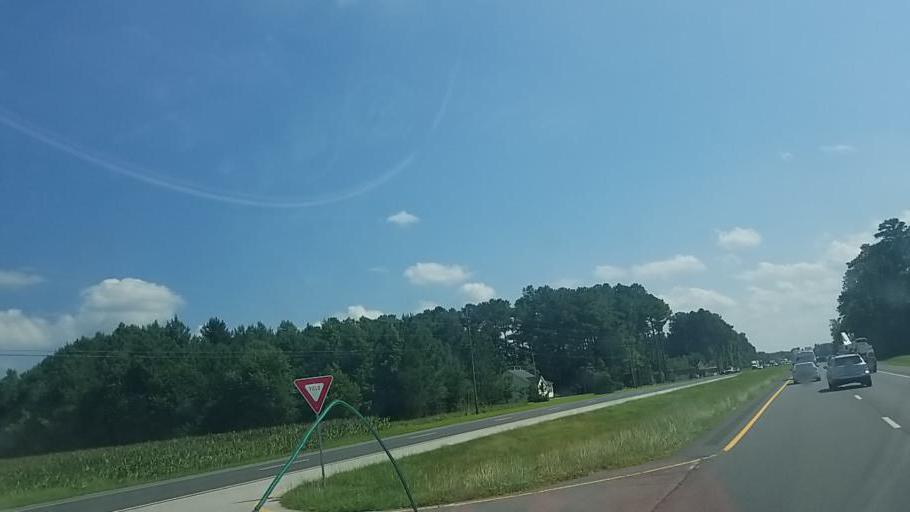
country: US
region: Delaware
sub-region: Sussex County
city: Milford
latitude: 38.8173
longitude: -75.4390
